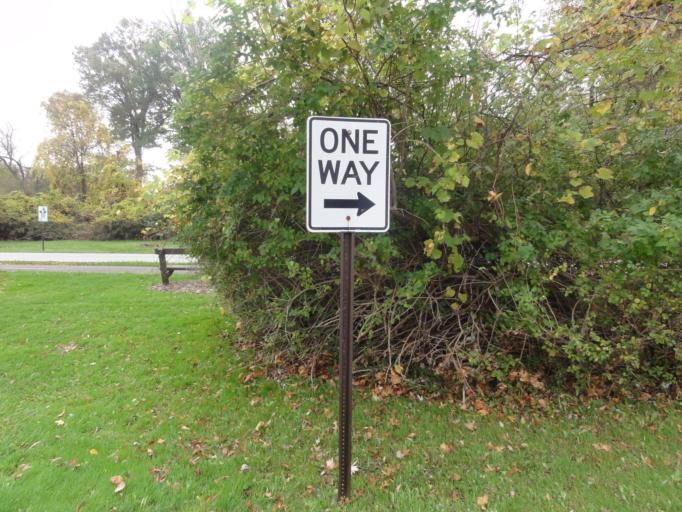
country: US
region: Ohio
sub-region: Cuyahoga County
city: Brook Park
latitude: 41.3833
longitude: -81.7858
